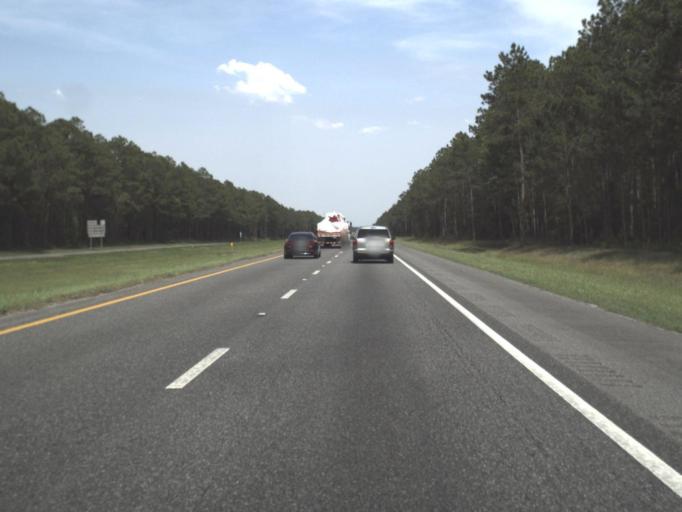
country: US
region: Florida
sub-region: Union County
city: Lake Butler
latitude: 30.2541
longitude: -82.3682
